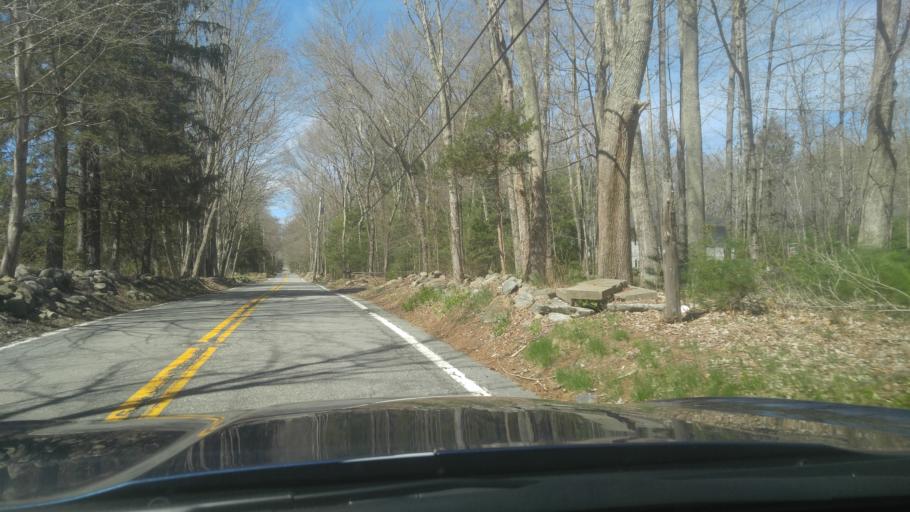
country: US
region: Rhode Island
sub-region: Washington County
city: Hope Valley
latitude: 41.5779
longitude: -71.7556
